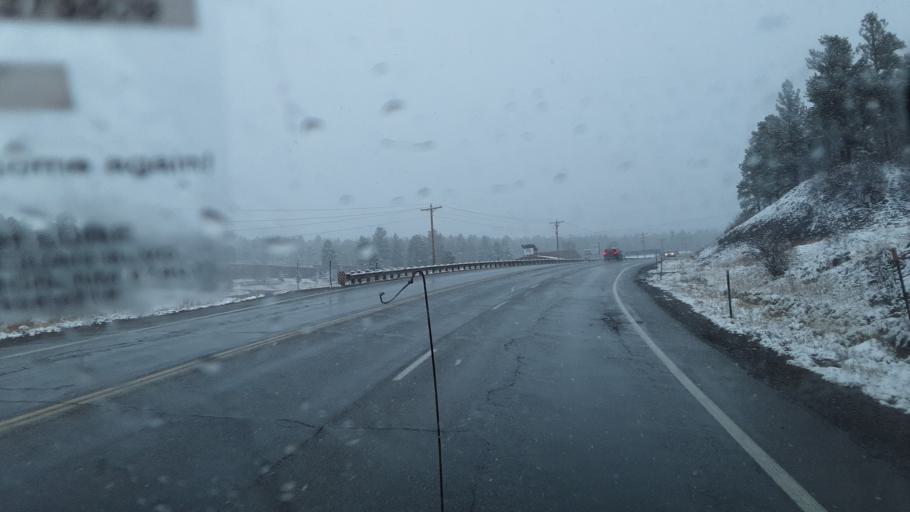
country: US
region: Colorado
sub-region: Archuleta County
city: Pagosa Springs
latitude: 37.2673
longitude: -107.0275
